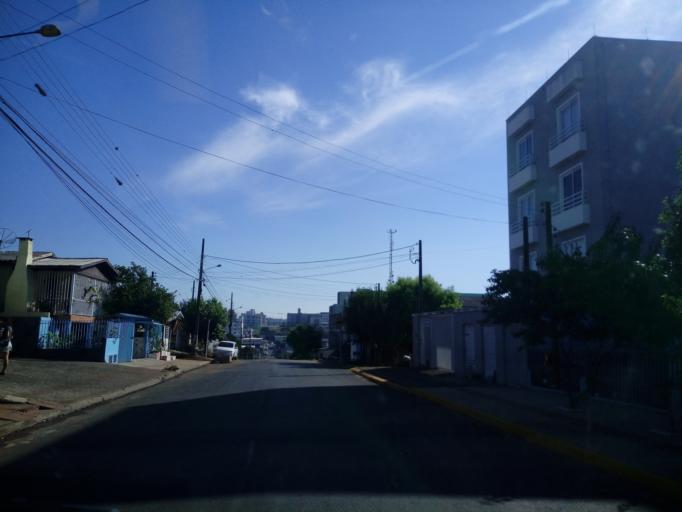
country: BR
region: Santa Catarina
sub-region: Chapeco
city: Chapeco
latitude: -27.1002
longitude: -52.6698
